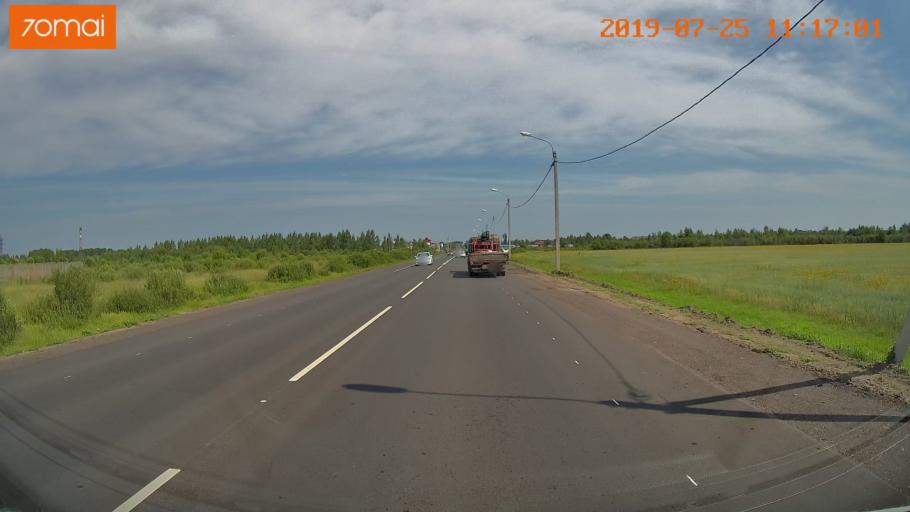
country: RU
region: Ivanovo
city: Privolzhsk
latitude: 57.3635
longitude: 41.2687
